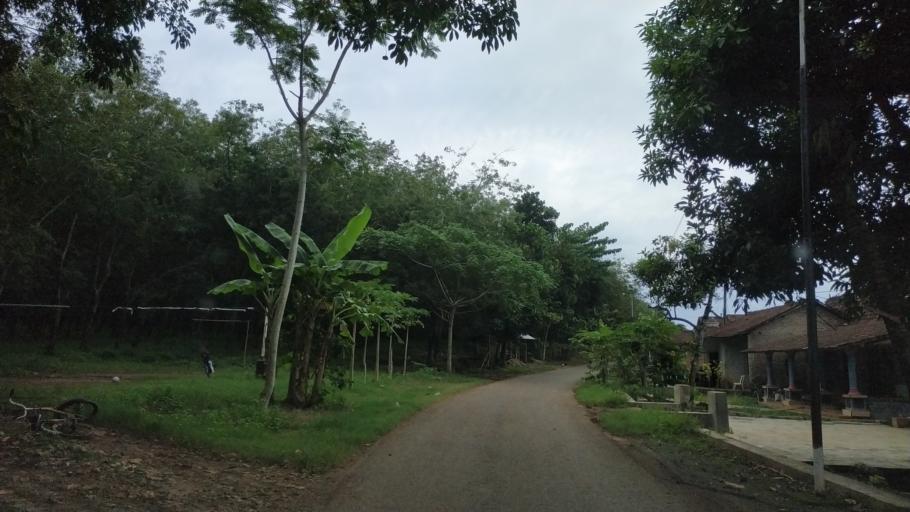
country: ID
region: Central Java
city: Krajan Tegalombo
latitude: -6.4344
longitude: 110.9822
